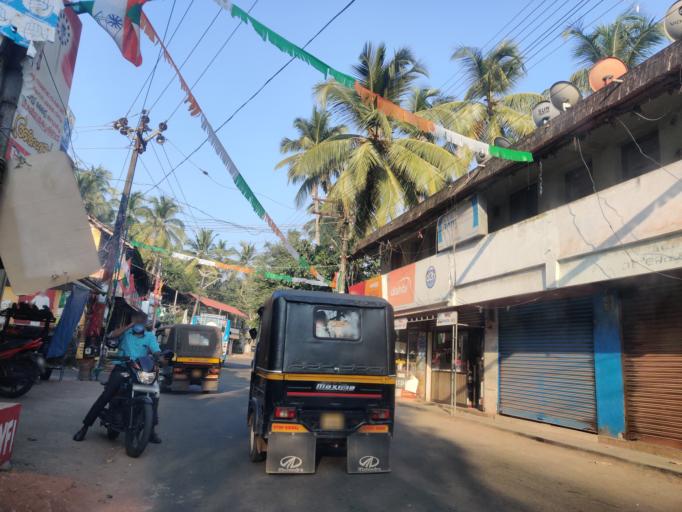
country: IN
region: Kerala
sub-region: Thrissur District
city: Kunnamkulam
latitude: 10.7341
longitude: 76.0199
